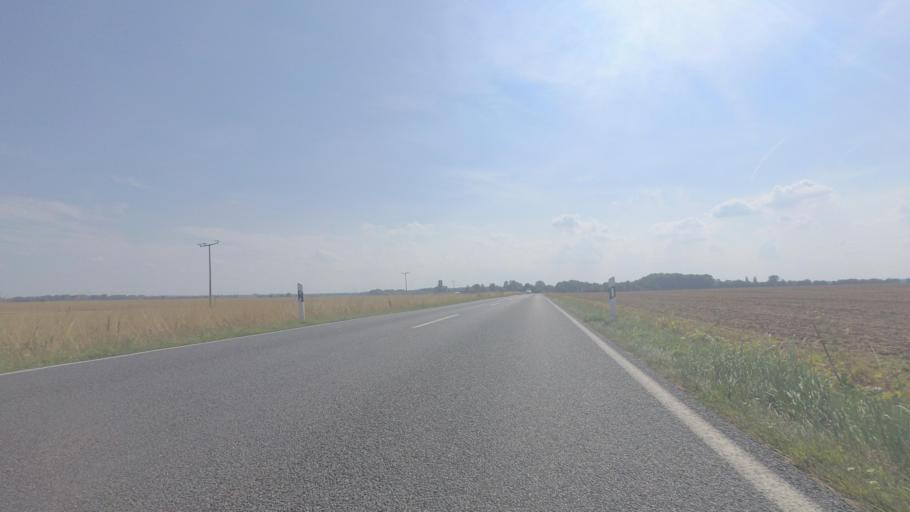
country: DE
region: Mecklenburg-Vorpommern
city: Wittenhagen
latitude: 54.1361
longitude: 13.1452
